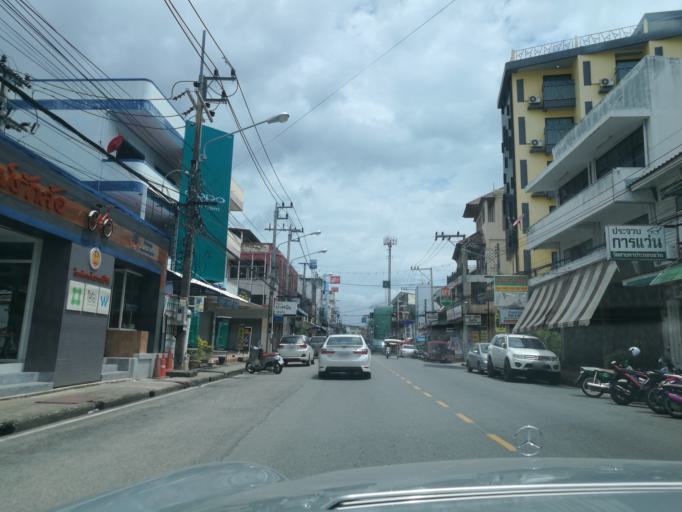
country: TH
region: Prachuap Khiri Khan
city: Prachuap Khiri Khan
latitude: 11.8006
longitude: 99.7986
